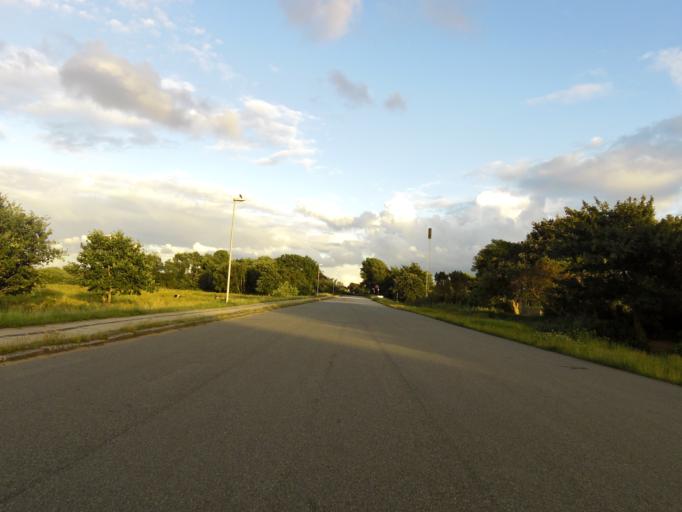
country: DK
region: South Denmark
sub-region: Esbjerg Kommune
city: Ribe
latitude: 55.3223
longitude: 8.7641
